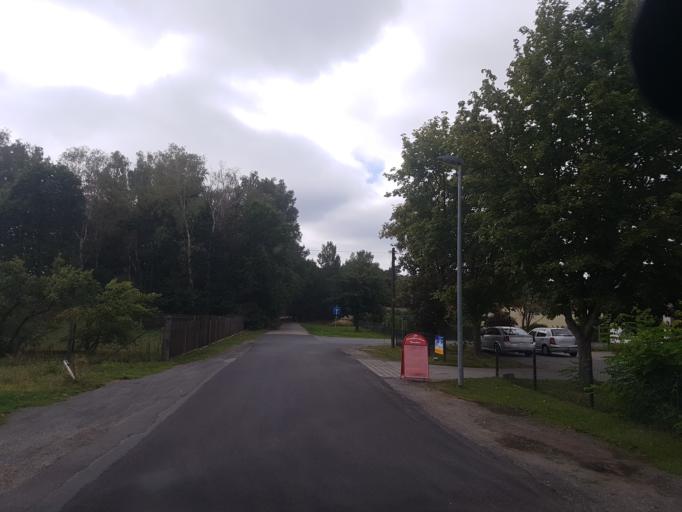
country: DE
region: Brandenburg
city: Bronkow
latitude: 51.6672
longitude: 13.9150
